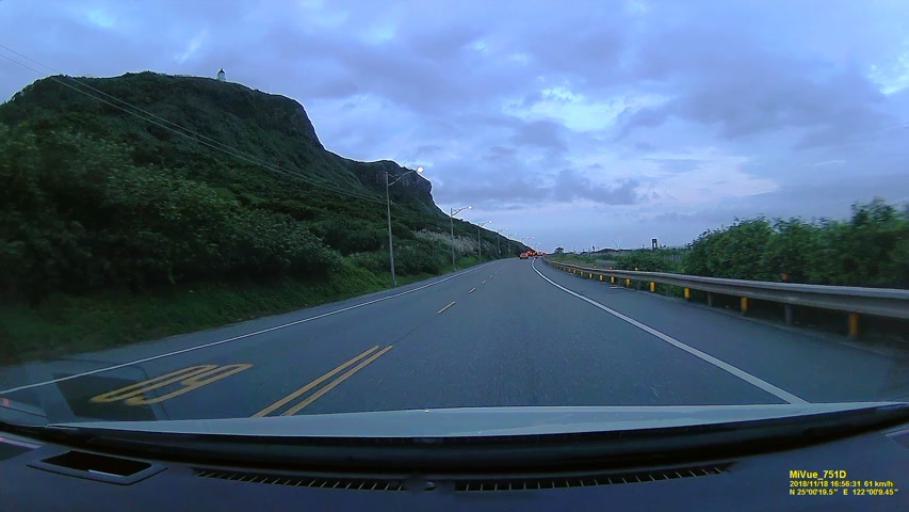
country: TW
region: Taiwan
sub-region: Keelung
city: Keelung
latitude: 25.0055
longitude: 122.0026
